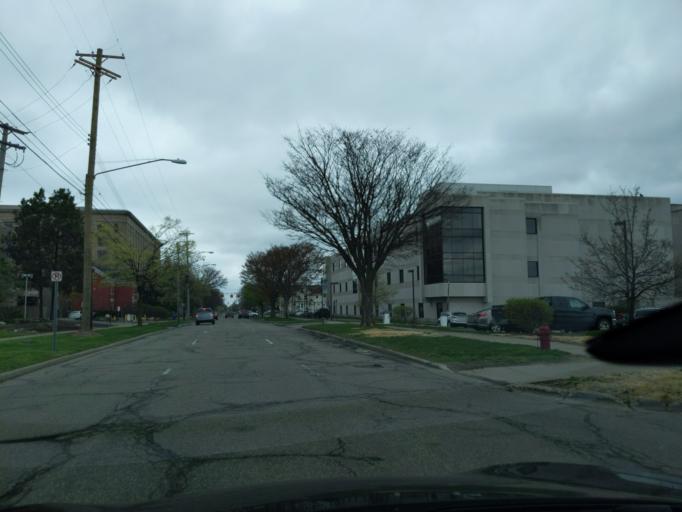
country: US
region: Michigan
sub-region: Ingham County
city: Lansing
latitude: 42.7287
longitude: -84.5570
